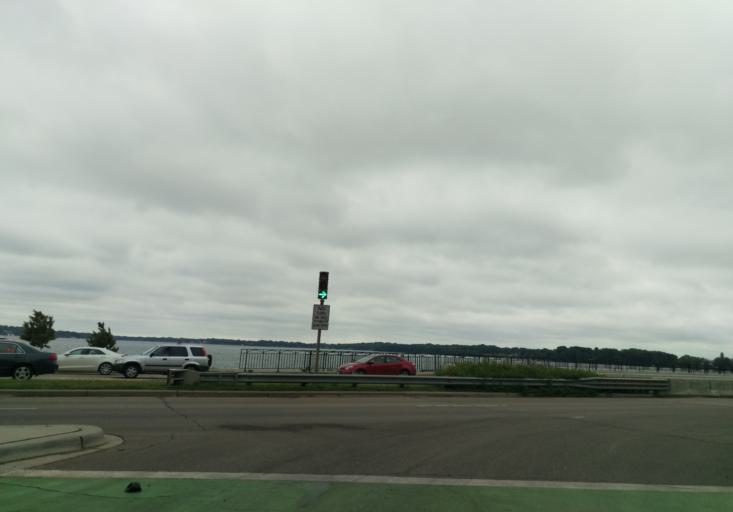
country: US
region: Wisconsin
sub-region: Dane County
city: Madison
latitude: 43.0669
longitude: -89.3861
